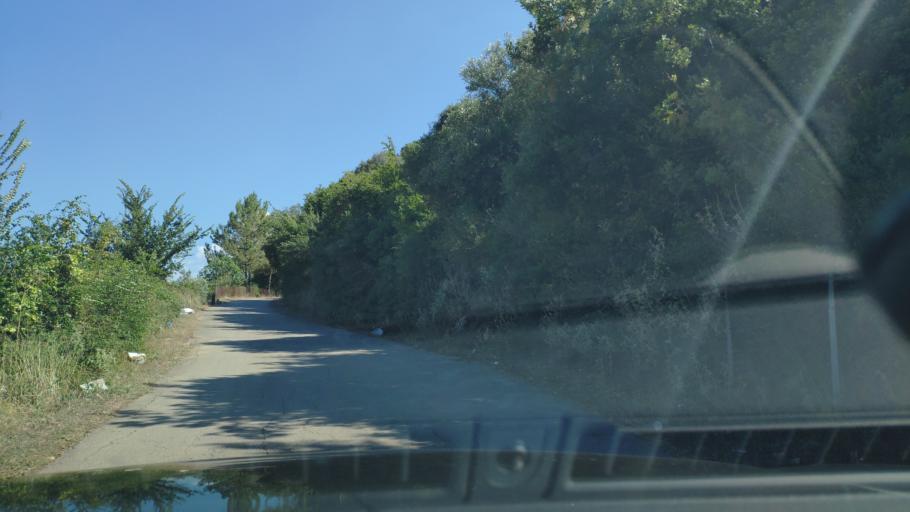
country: GR
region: West Greece
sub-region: Nomos Aitolias kai Akarnanias
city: Katouna
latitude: 38.7953
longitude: 21.1143
